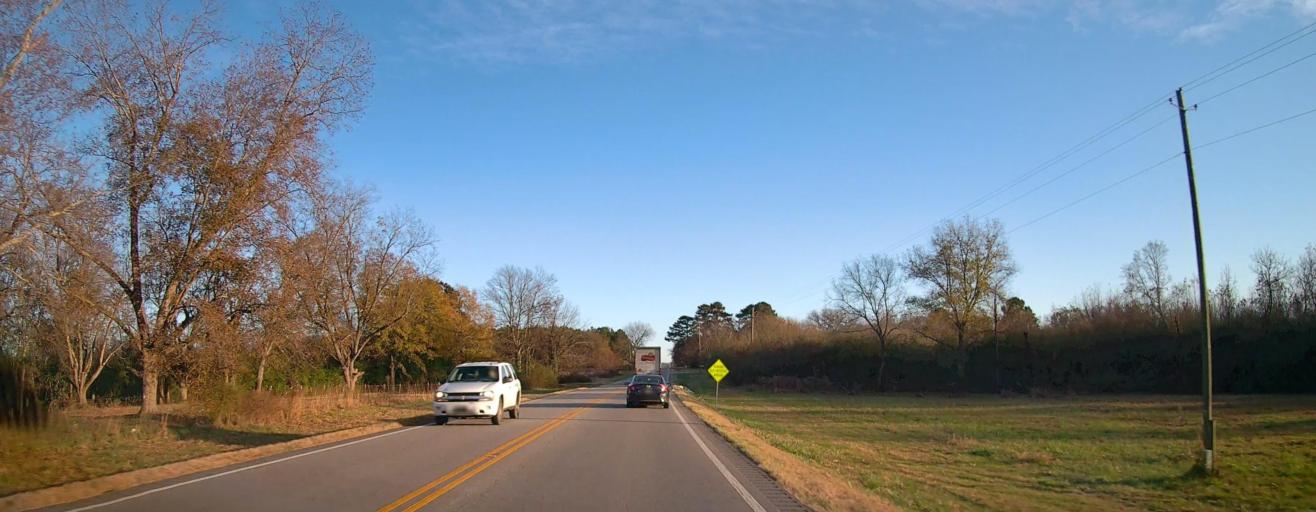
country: US
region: Alabama
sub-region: Blount County
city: Oneonta
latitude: 34.0937
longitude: -86.3553
